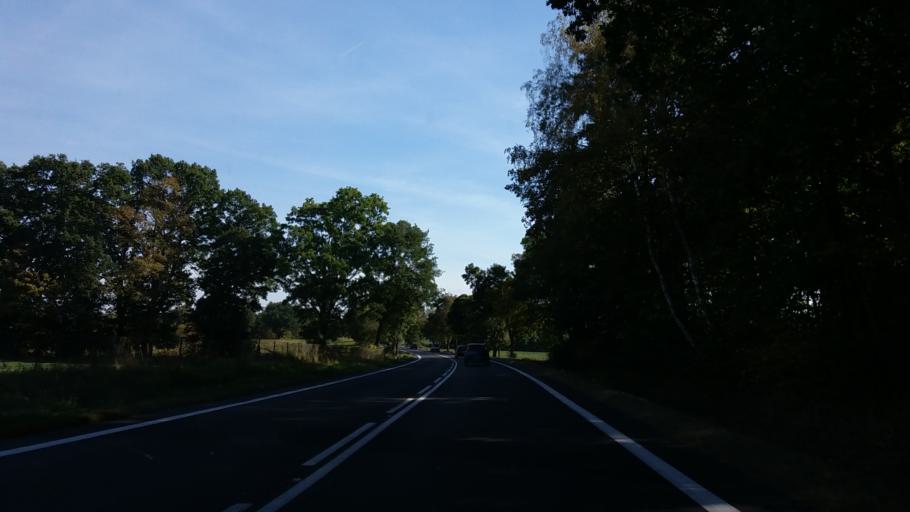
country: PL
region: Greater Poland Voivodeship
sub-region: Powiat miedzychodzki
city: Kwilcz
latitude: 52.5386
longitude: 16.1406
